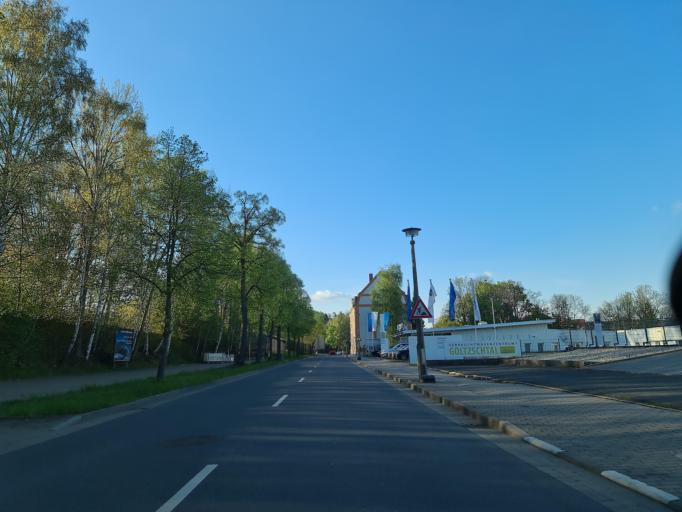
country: DE
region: Saxony
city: Auerbach
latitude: 50.5124
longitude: 12.3926
